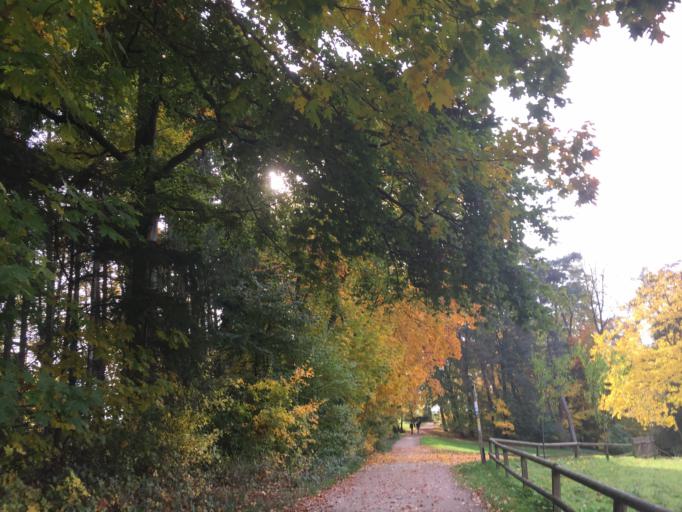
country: DE
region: Hesse
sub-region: Regierungsbezirk Darmstadt
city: Bensheim
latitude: 49.6982
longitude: 8.6386
